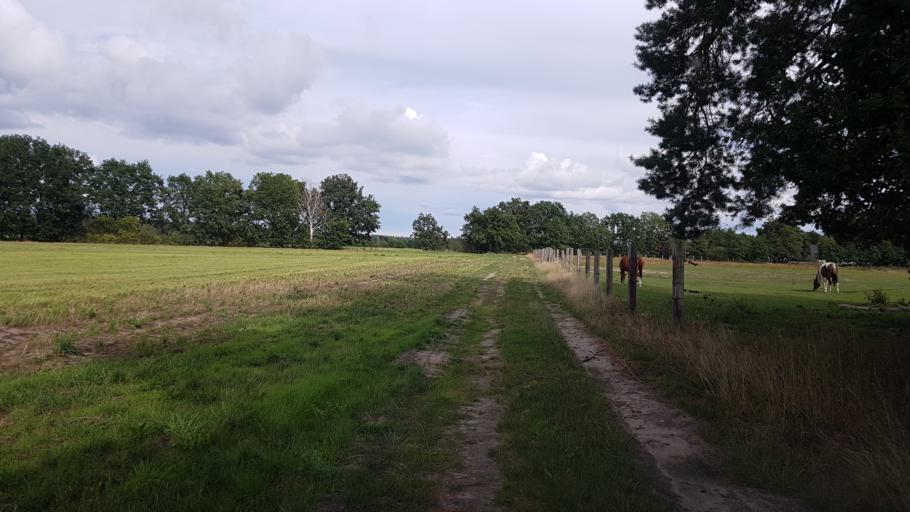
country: DE
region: Brandenburg
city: Doberlug-Kirchhain
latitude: 51.6379
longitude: 13.5994
